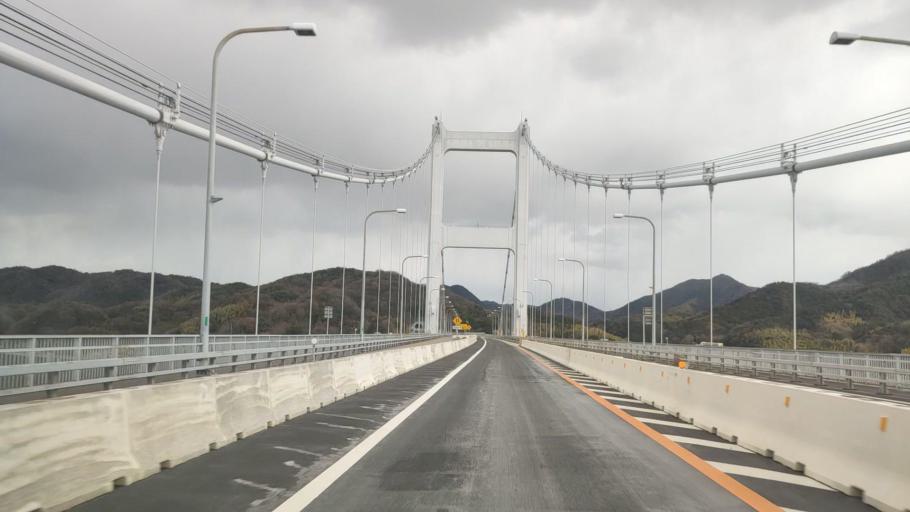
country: JP
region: Hiroshima
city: Innoshima
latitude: 34.1261
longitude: 133.0129
